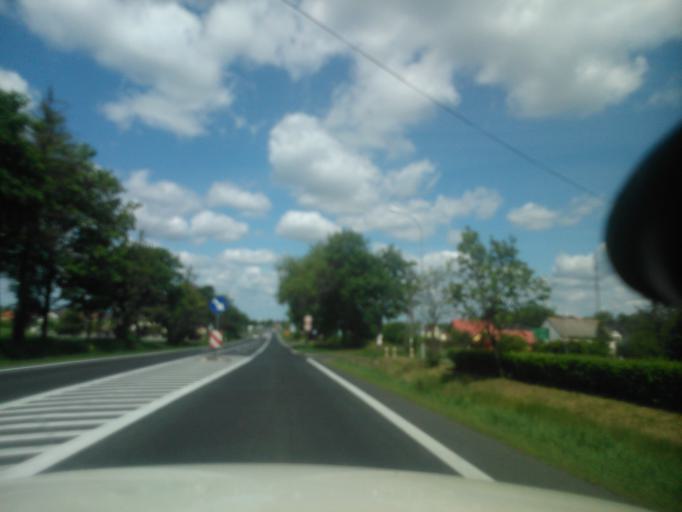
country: PL
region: Kujawsko-Pomorskie
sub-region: Powiat torunski
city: Lubicz Gorny
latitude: 53.0131
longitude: 18.8227
